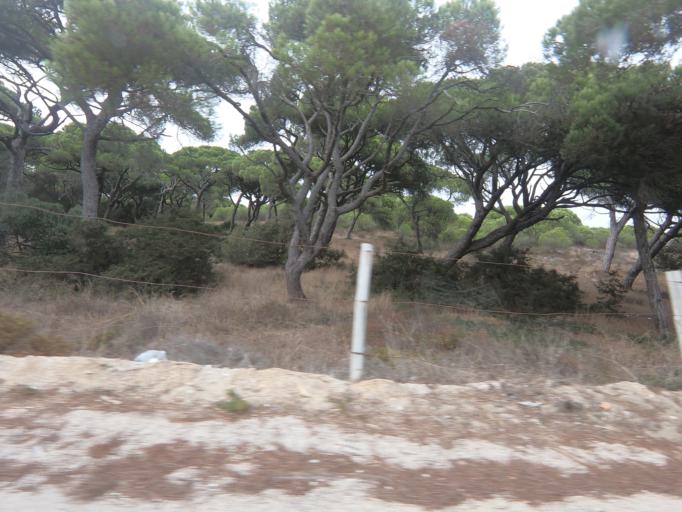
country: PT
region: Setubal
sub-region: Almada
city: Charneca
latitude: 38.5751
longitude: -9.1913
